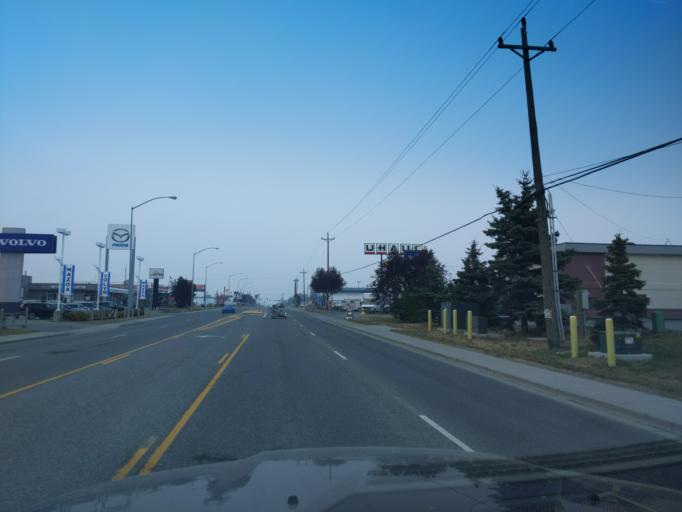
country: US
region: Alaska
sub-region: Anchorage Municipality
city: Anchorage
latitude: 61.1764
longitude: -149.8681
